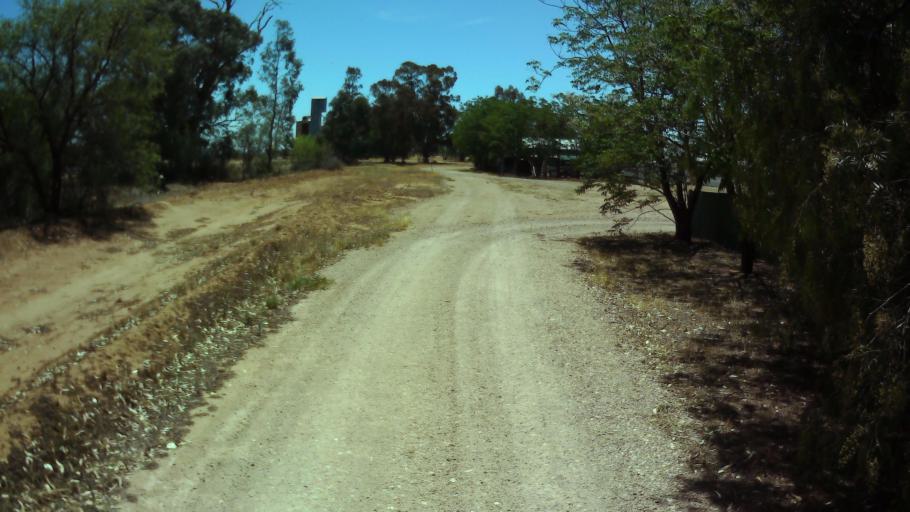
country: AU
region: New South Wales
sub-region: Weddin
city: Grenfell
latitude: -33.8435
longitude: 147.7425
